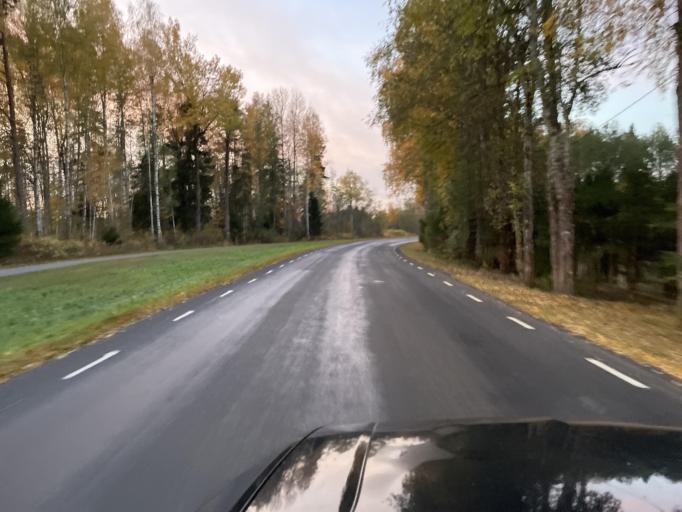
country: EE
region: Harju
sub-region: Nissi vald
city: Riisipere
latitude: 59.2363
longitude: 24.2442
